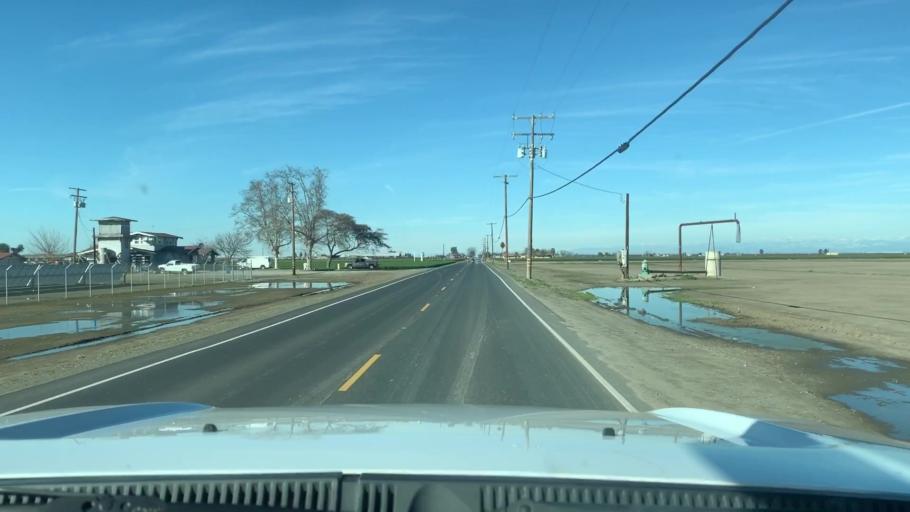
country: US
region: California
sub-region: Kings County
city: Corcoran
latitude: 36.1898
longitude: -119.4932
